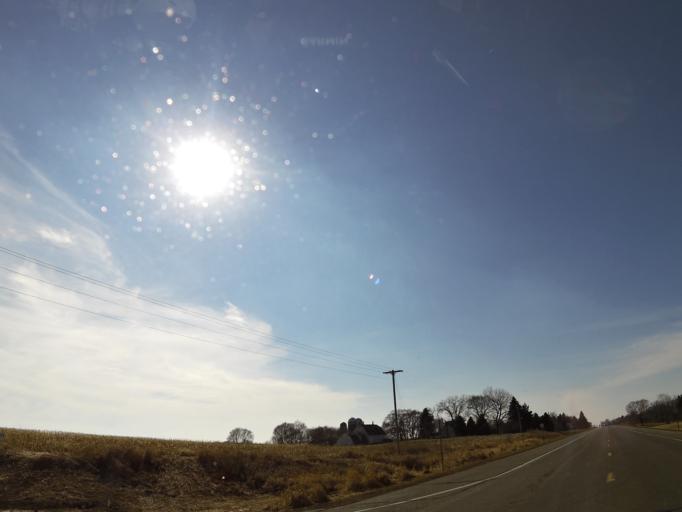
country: US
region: Minnesota
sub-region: Scott County
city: Prior Lake
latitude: 44.6889
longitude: -93.4808
